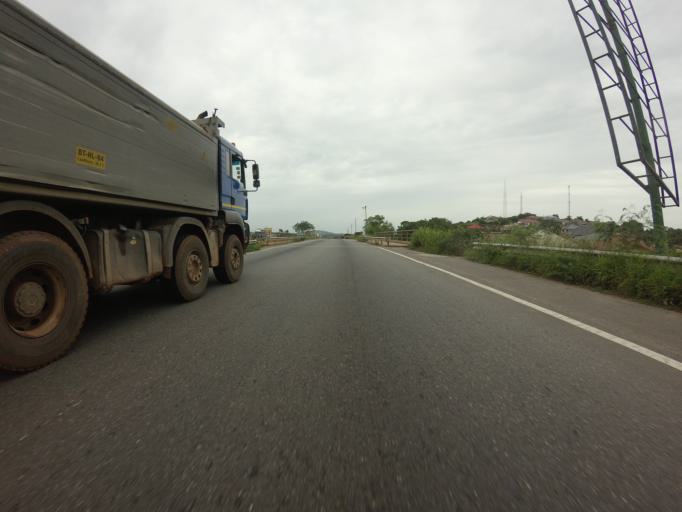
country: GH
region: Eastern
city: Nsawam
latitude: 5.8177
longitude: -0.3641
